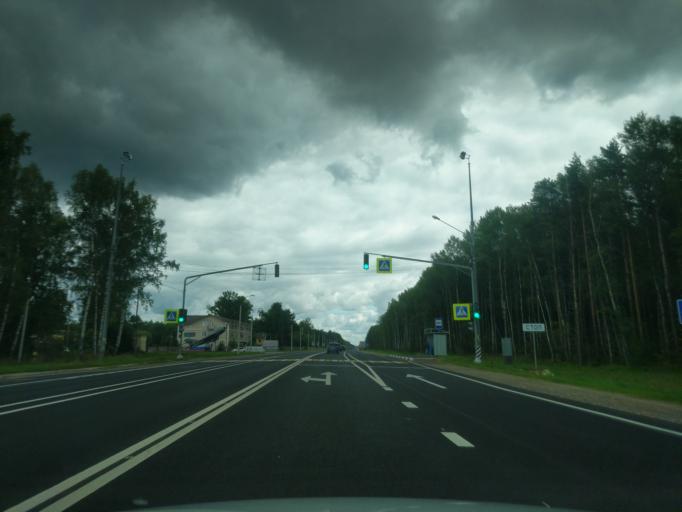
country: RU
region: Jaroslavl
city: Tunoshna
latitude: 57.5460
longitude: 40.1570
